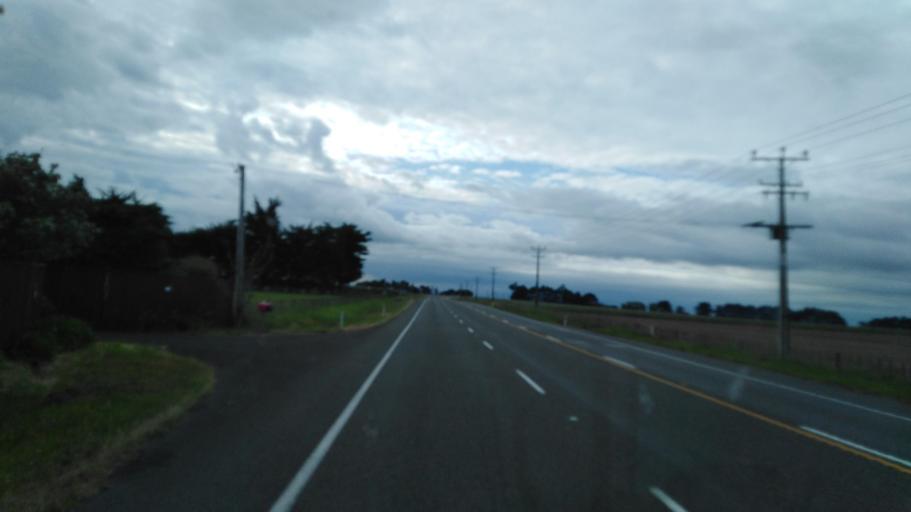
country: NZ
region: Manawatu-Wanganui
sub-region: Rangitikei District
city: Bulls
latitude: -40.1303
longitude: 175.3591
